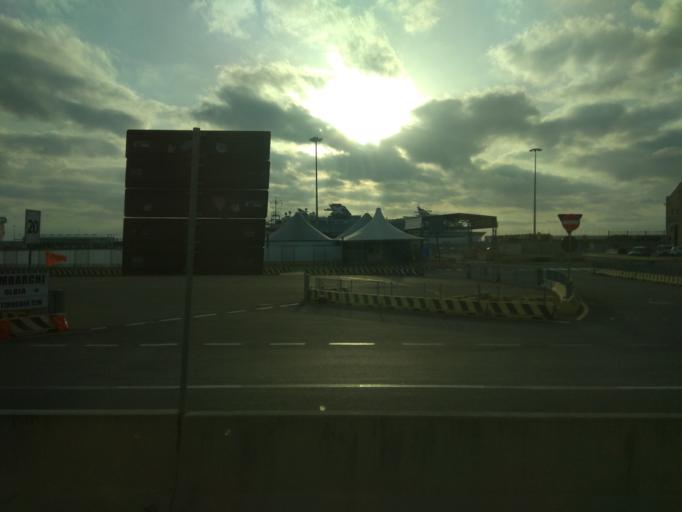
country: IT
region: Latium
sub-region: Citta metropolitana di Roma Capitale
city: Civitavecchia
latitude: 42.1010
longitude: 11.7831
